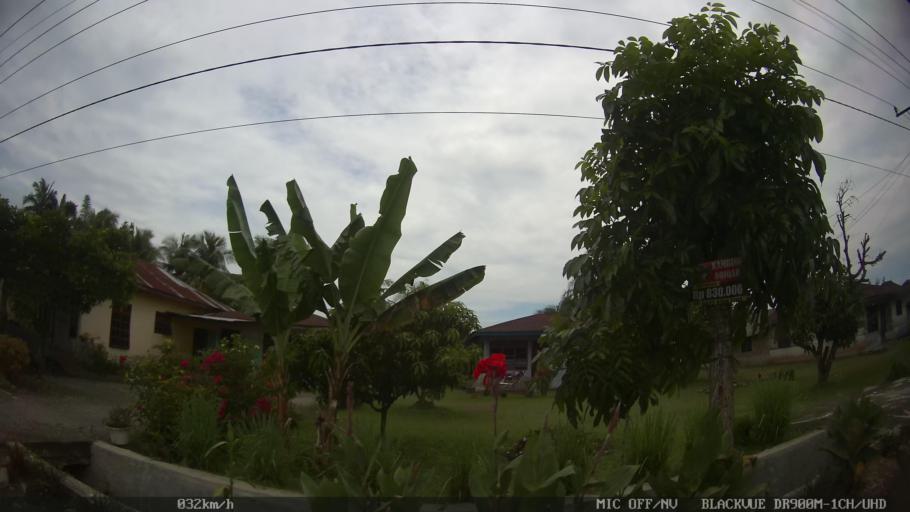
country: ID
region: North Sumatra
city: Binjai
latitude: 3.6332
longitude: 98.5543
